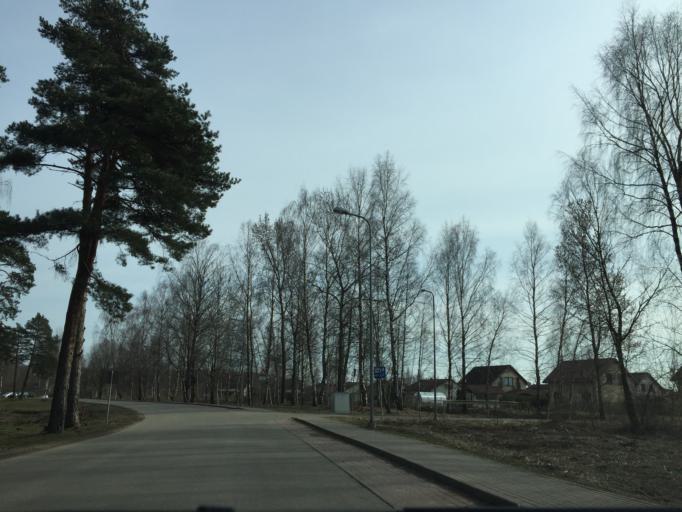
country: LV
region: Kekava
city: Balozi
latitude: 56.8735
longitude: 24.1291
